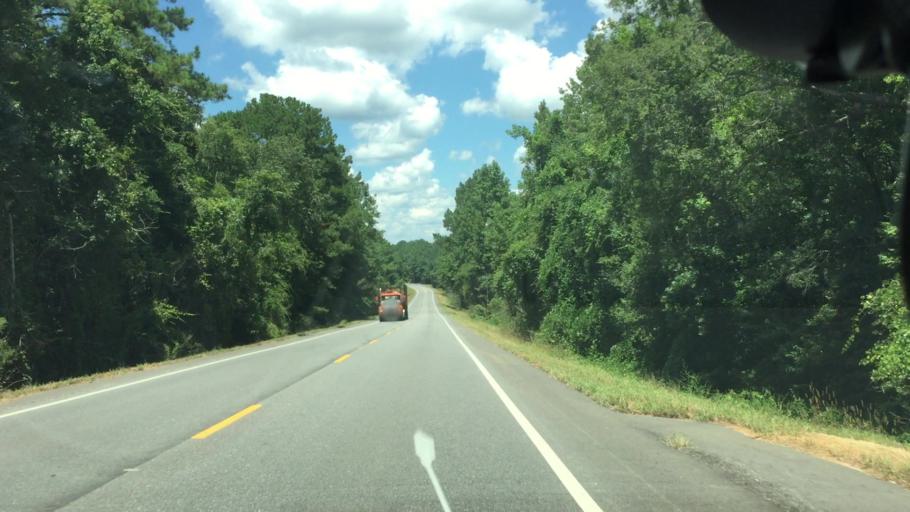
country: US
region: Alabama
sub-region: Coffee County
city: New Brockton
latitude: 31.4592
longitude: -85.8981
